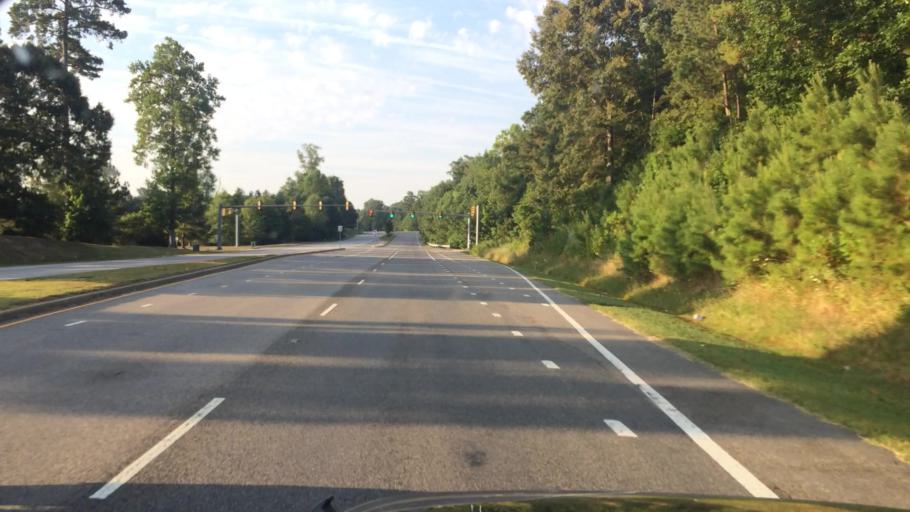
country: US
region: Virginia
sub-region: James City County
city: Williamsburg
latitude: 37.3378
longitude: -76.7378
